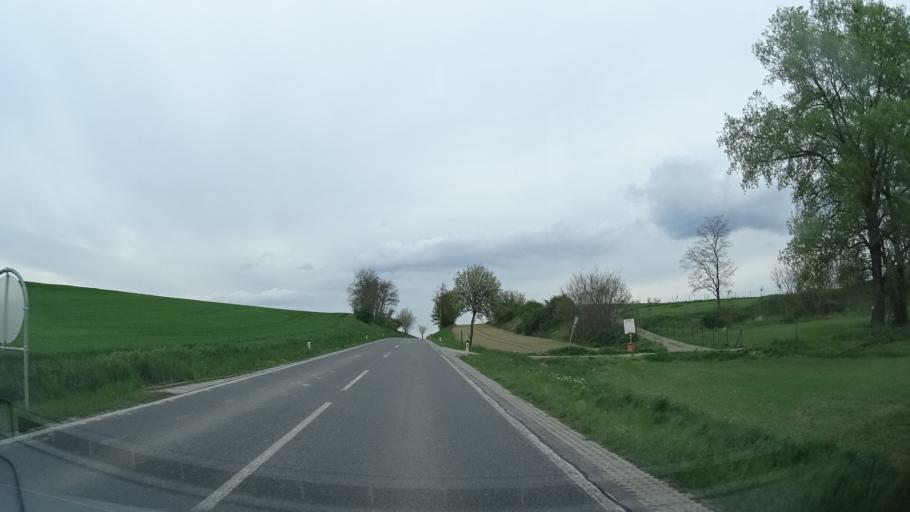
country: AT
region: Lower Austria
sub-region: Politischer Bezirk Korneuburg
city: Harmannsdorf
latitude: 48.3682
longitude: 16.3570
